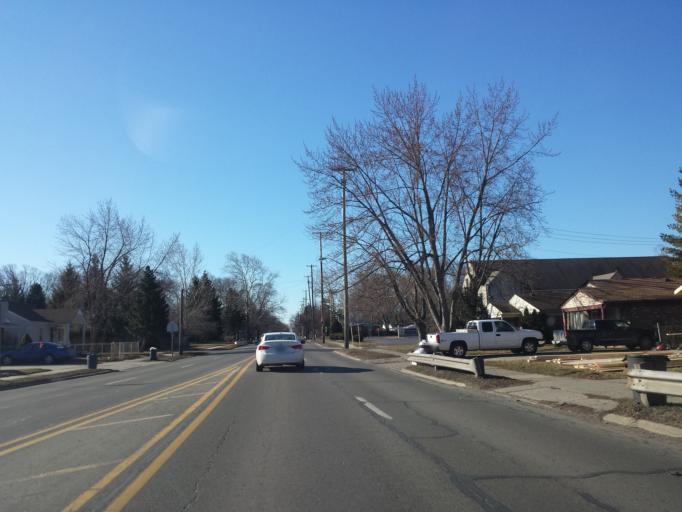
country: US
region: Michigan
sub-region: Oakland County
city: Clawson
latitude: 42.5180
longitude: -83.1456
